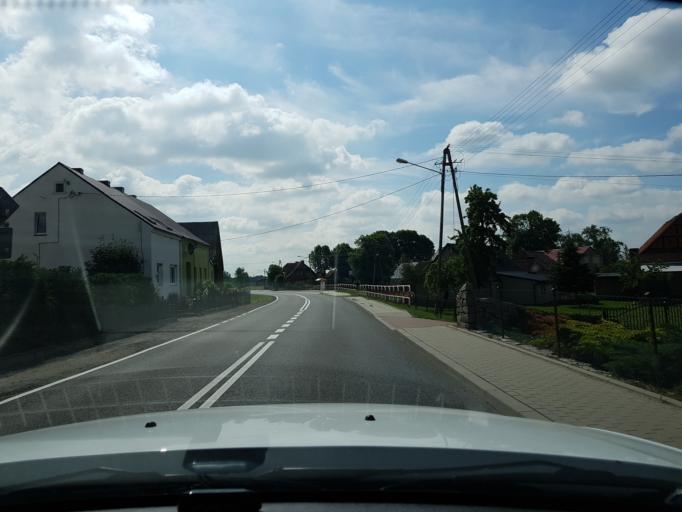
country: PL
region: West Pomeranian Voivodeship
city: Trzcinsko Zdroj
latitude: 52.9794
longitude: 14.7175
